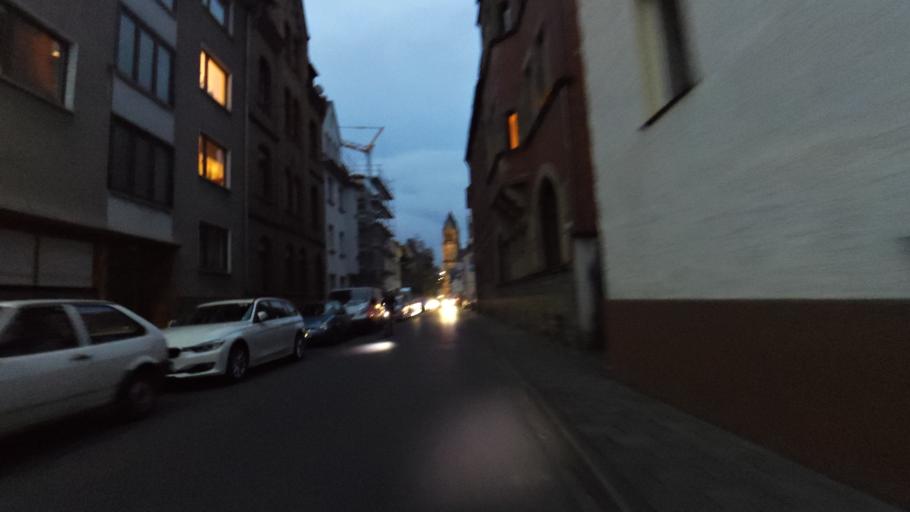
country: DE
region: Rheinland-Pfalz
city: Koblenz
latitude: 50.3466
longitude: 7.6033
